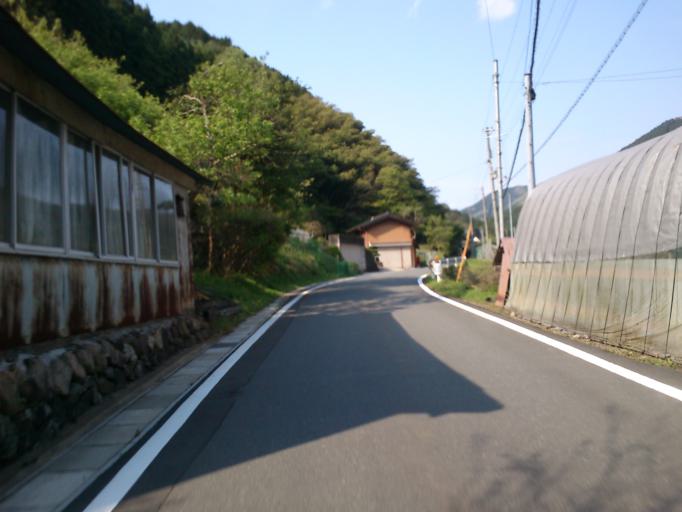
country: JP
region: Kyoto
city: Fukuchiyama
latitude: 35.3490
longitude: 135.0105
